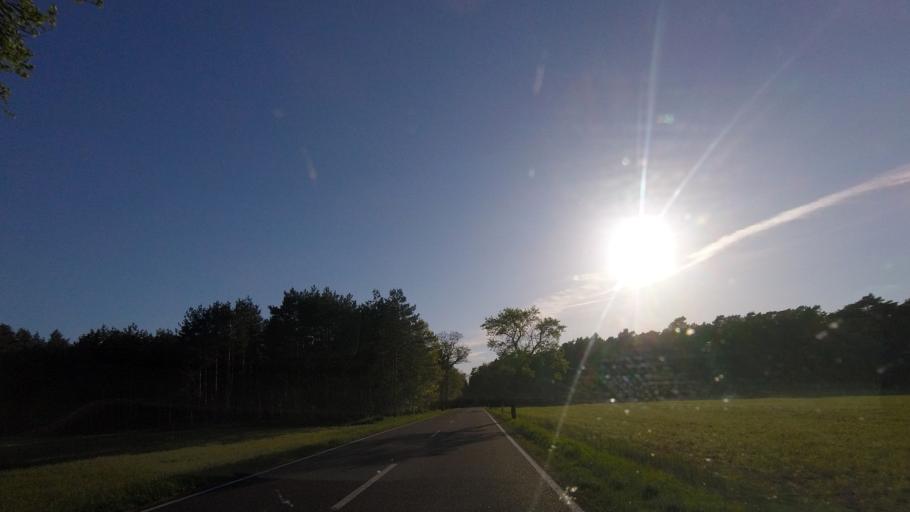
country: DE
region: Brandenburg
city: Baruth
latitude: 51.9963
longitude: 13.3990
